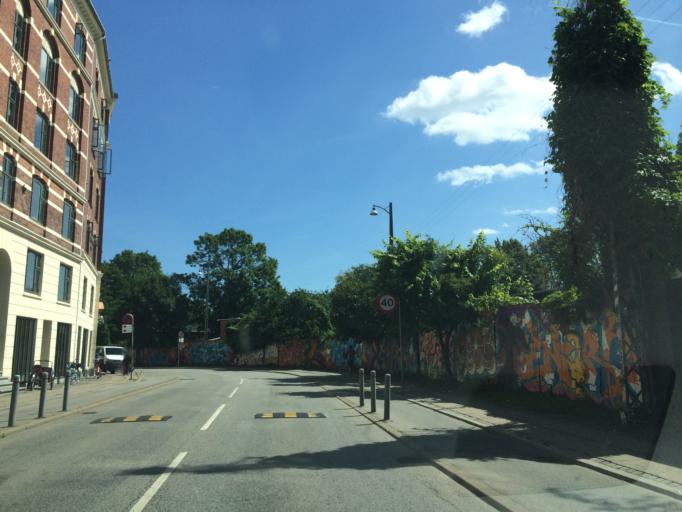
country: DK
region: Capital Region
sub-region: Kobenhavn
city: Christianshavn
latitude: 55.6745
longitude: 12.5981
